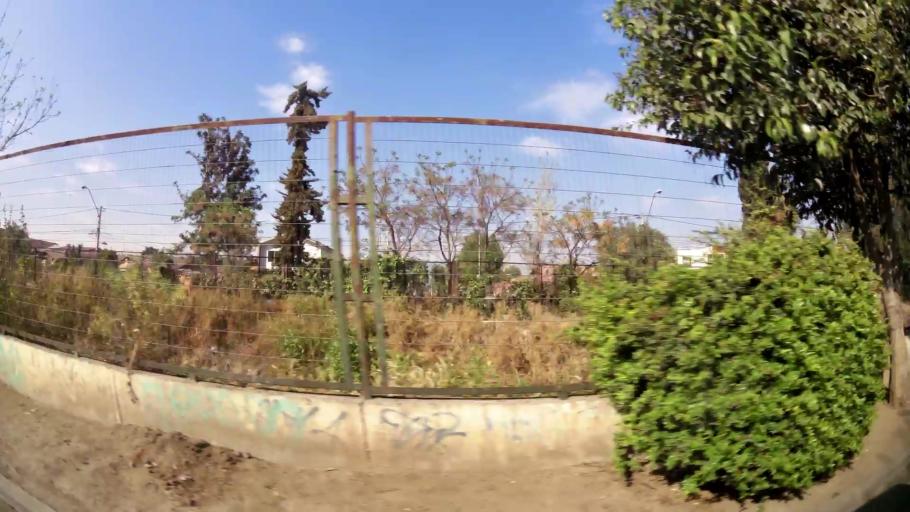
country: CL
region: Santiago Metropolitan
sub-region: Provincia de Santiago
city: Lo Prado
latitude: -33.4666
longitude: -70.7473
